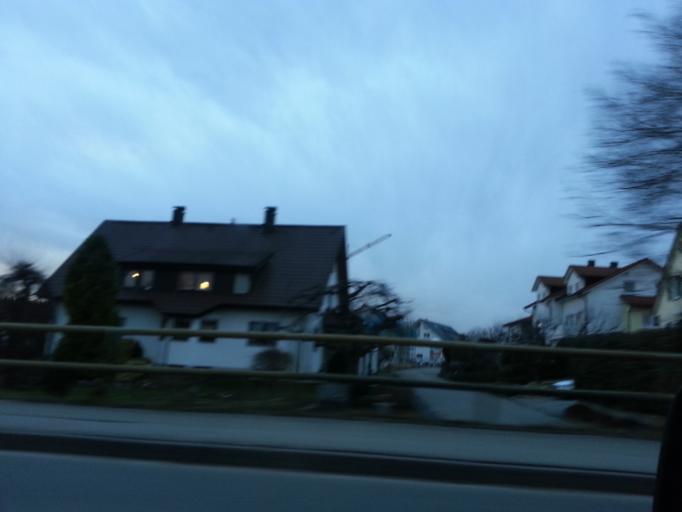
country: DE
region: Baden-Wuerttemberg
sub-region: Tuebingen Region
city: Markdorf
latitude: 47.6989
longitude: 9.3985
